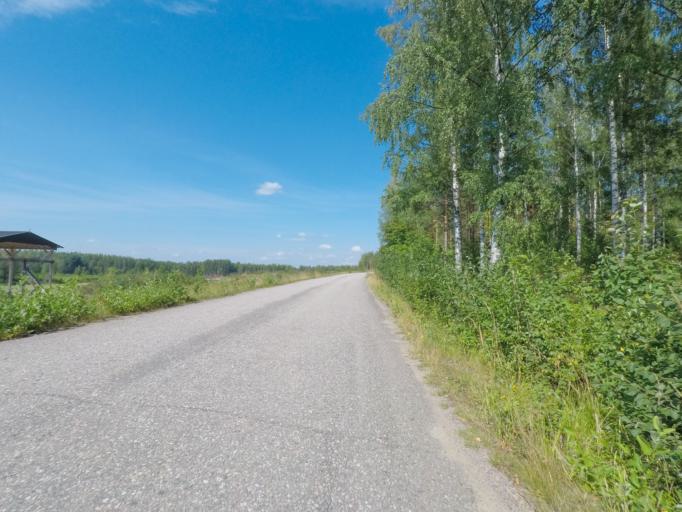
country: FI
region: Southern Savonia
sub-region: Mikkeli
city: Puumala
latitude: 61.4139
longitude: 28.0920
